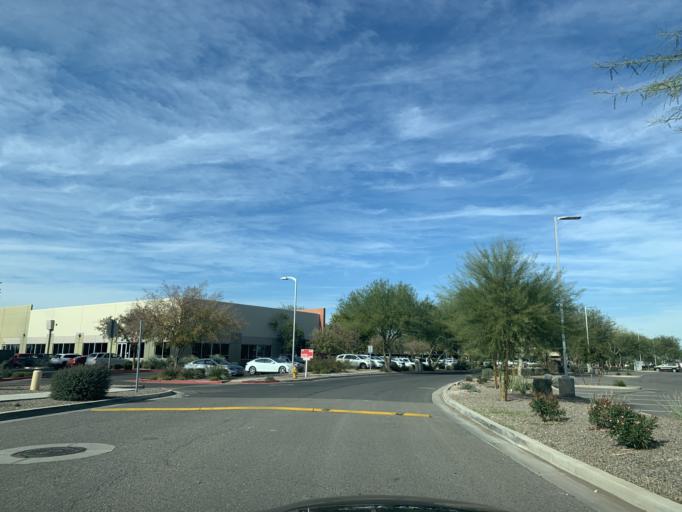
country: US
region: Arizona
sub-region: Maricopa County
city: Chandler
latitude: 33.2752
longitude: -111.7836
